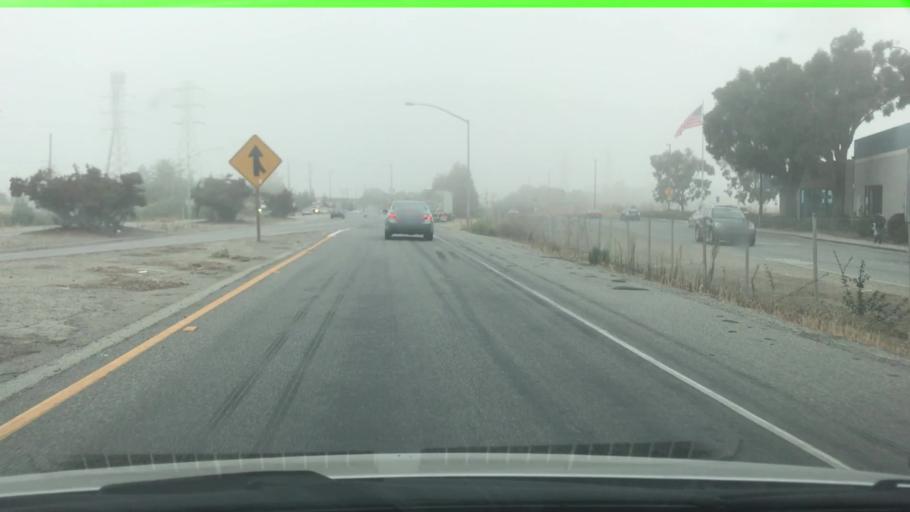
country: US
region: California
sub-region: San Mateo County
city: North Fair Oaks
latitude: 37.4907
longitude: -122.2118
